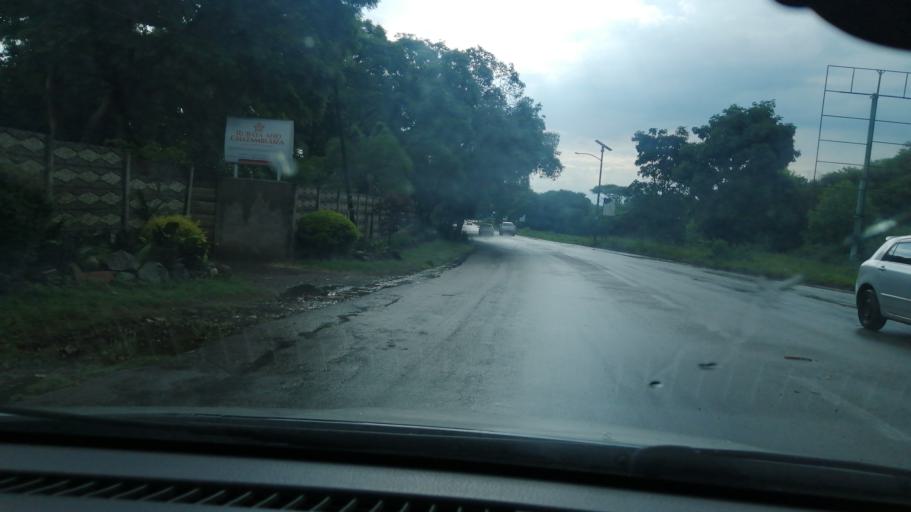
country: ZW
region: Harare
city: Harare
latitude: -17.7899
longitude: 31.0622
